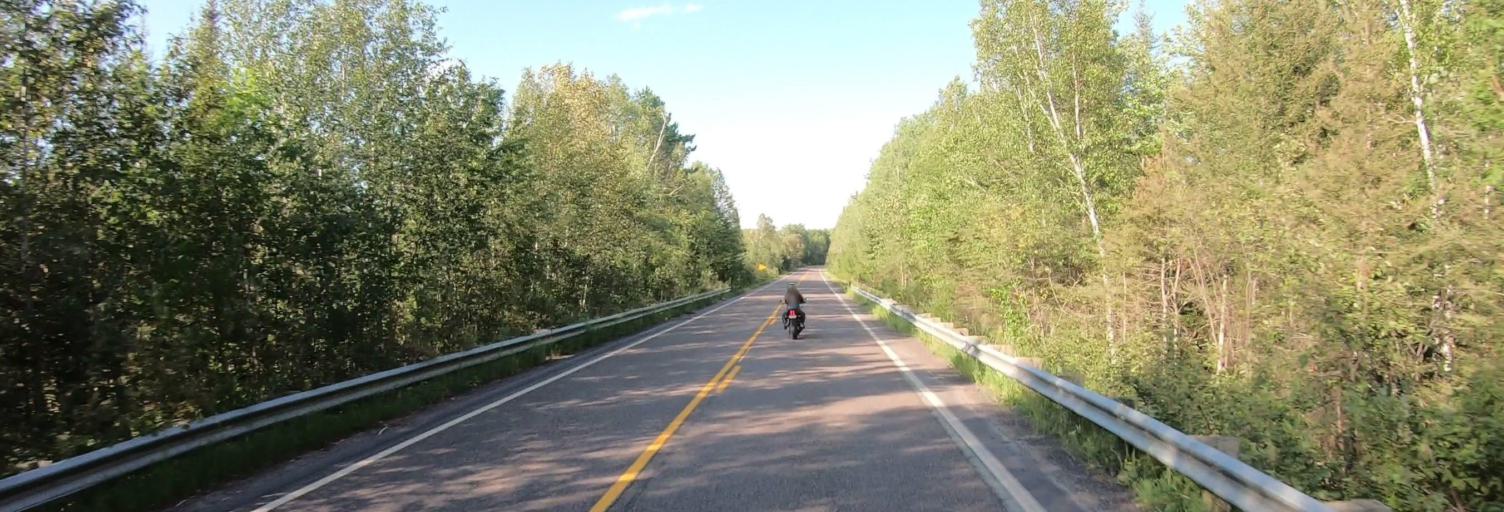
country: US
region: Minnesota
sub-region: Saint Louis County
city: Ely
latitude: 47.9484
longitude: -91.6484
